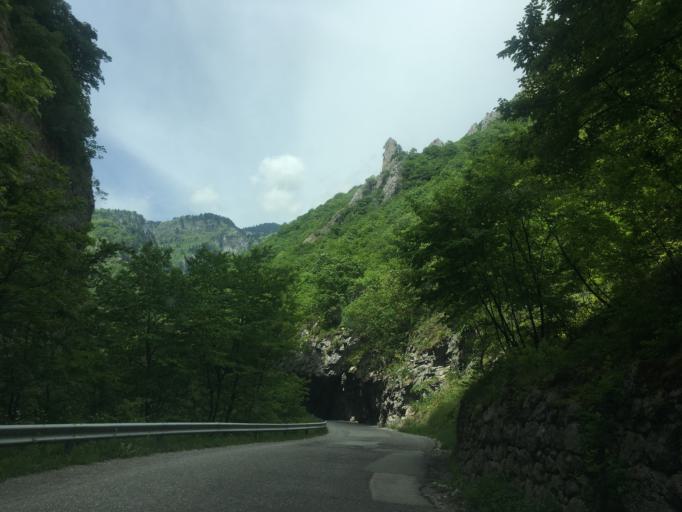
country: XK
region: Pec
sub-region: Komuna e Pejes
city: Peje
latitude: 42.6653
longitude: 20.2257
